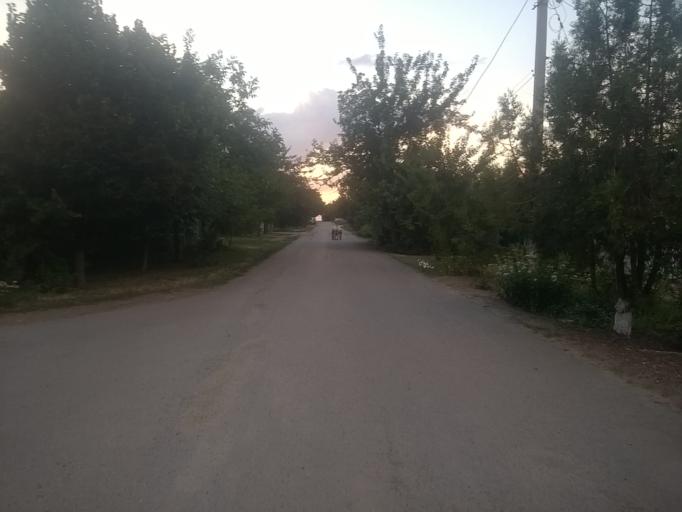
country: RU
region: Rostov
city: Donetsk
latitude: 48.3329
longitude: 39.9555
